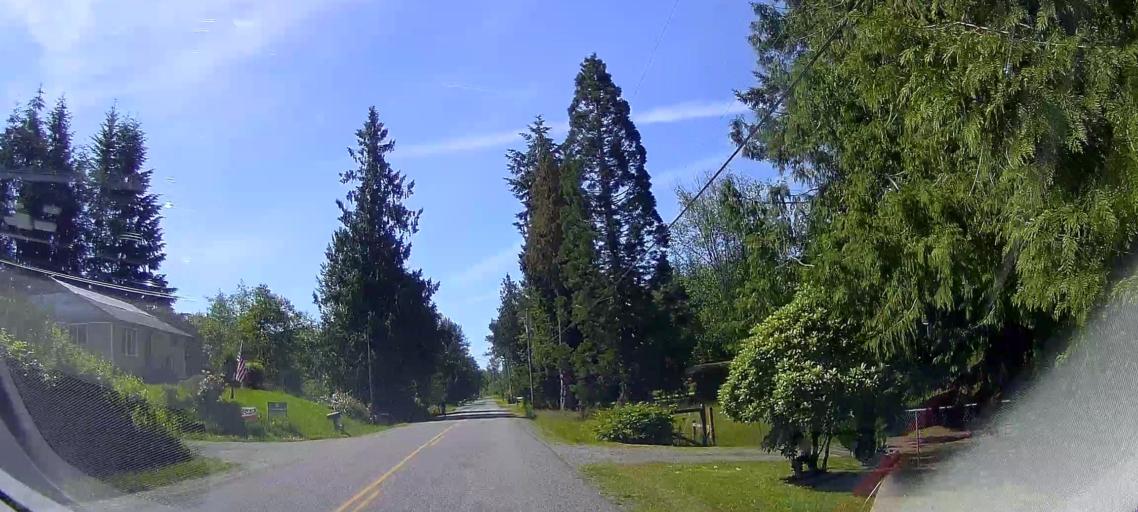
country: US
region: Washington
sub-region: Skagit County
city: Sedro-Woolley
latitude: 48.5464
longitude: -122.2480
